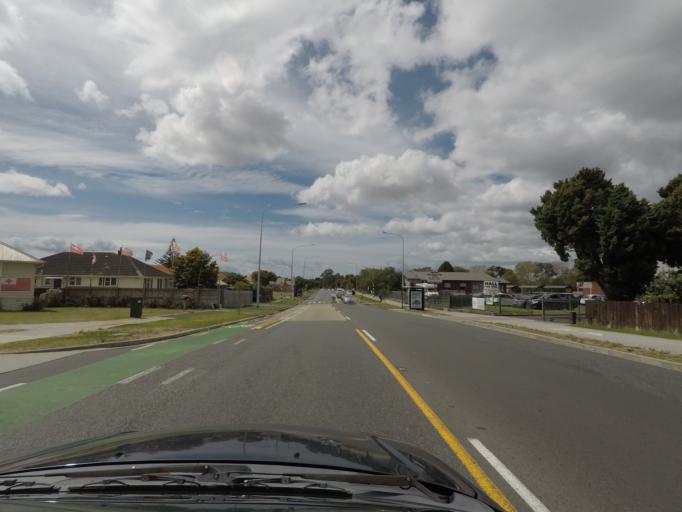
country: NZ
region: Auckland
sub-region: Auckland
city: Auckland
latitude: -36.9033
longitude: 174.7290
